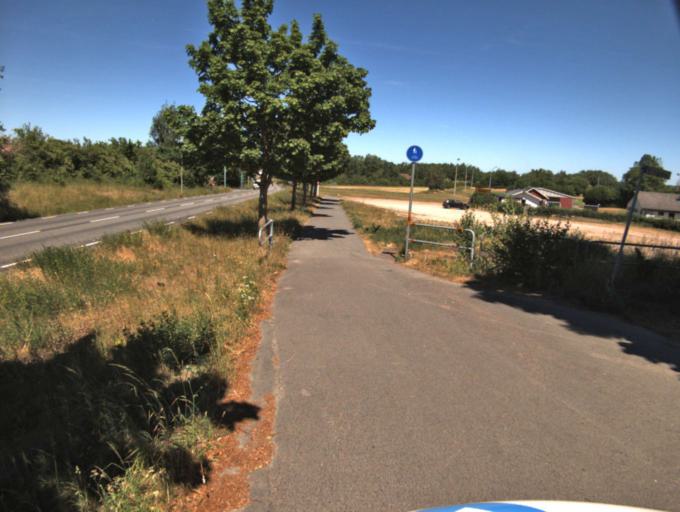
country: SE
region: Skane
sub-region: Kristianstads Kommun
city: Onnestad
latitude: 56.0502
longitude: 14.0223
